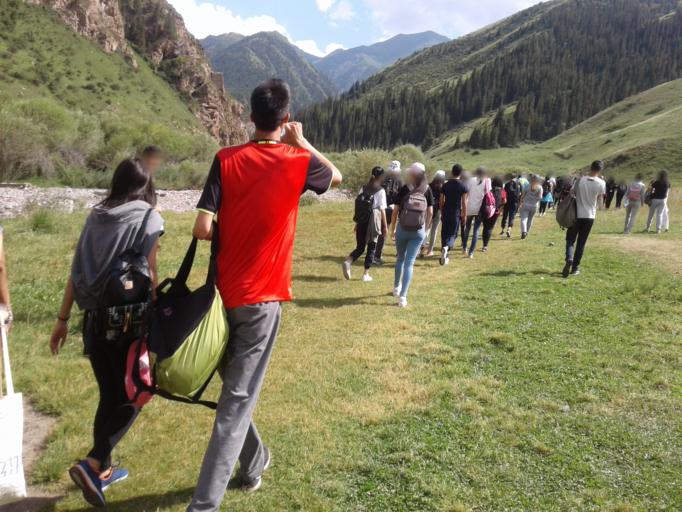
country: KG
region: Naryn
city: Naryn
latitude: 41.4595
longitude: 76.4533
